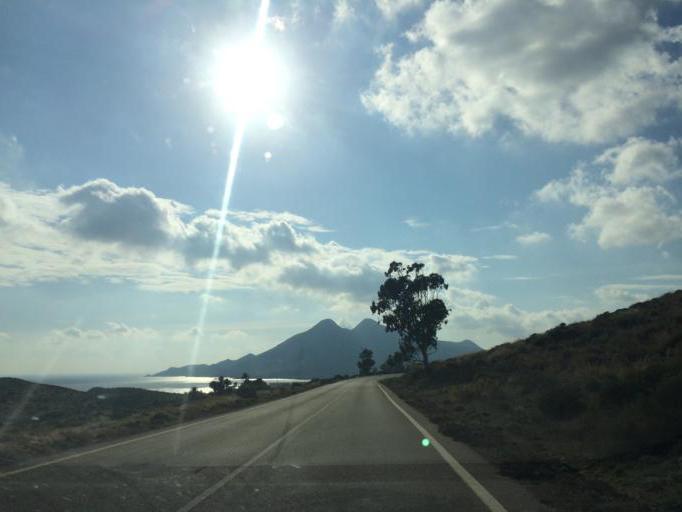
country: ES
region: Andalusia
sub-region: Provincia de Almeria
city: San Jose
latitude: 36.8239
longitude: -2.0478
